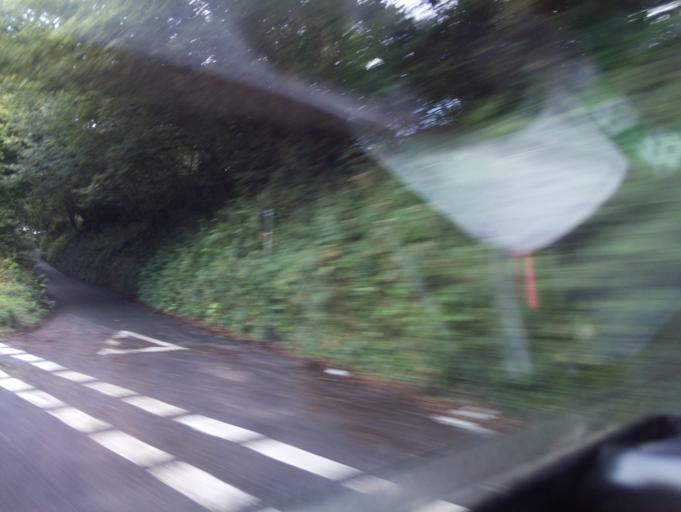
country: GB
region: England
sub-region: Devon
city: Modbury
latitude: 50.3416
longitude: -3.8759
